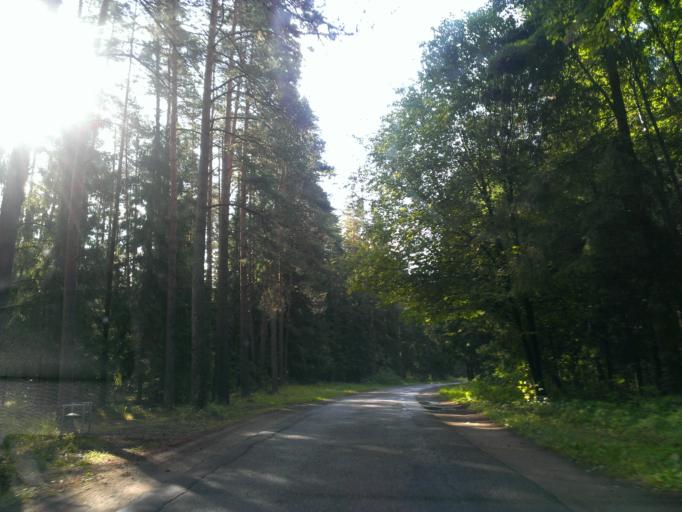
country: LV
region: Incukalns
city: Vangazi
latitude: 57.0985
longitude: 24.5332
